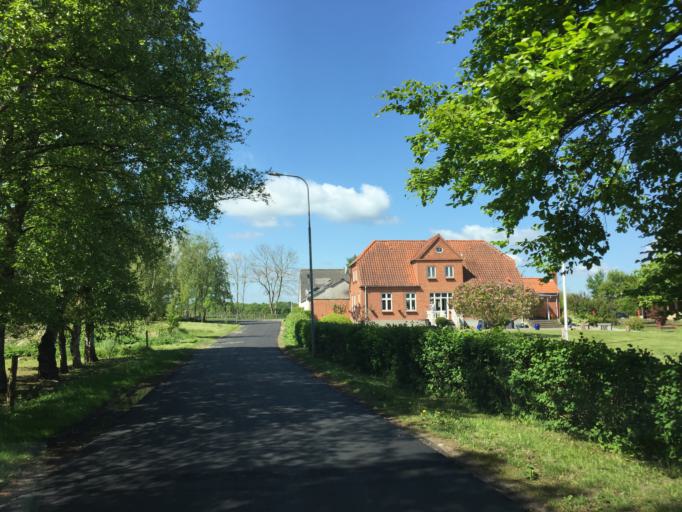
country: DK
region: South Denmark
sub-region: Middelfart Kommune
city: Brenderup
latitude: 55.5176
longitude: 10.0026
